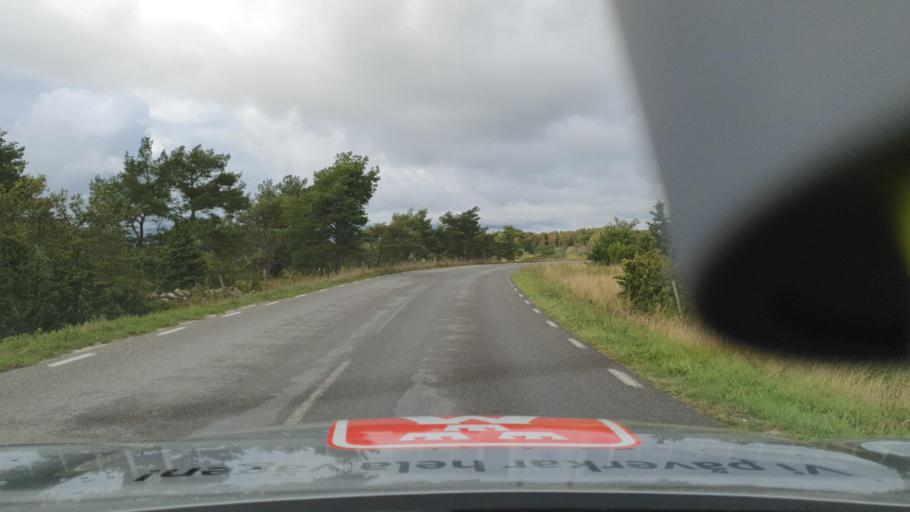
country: SE
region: Gotland
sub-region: Gotland
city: Hemse
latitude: 57.0219
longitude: 18.2630
